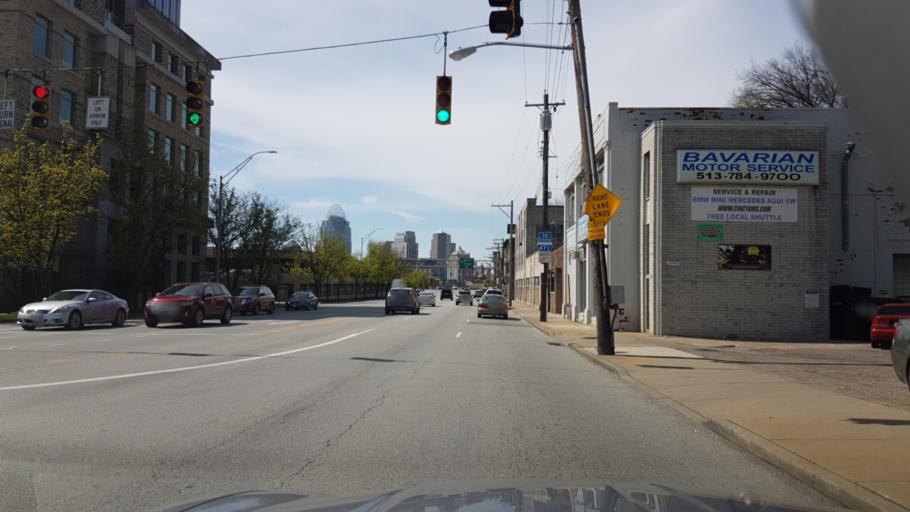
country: US
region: Kentucky
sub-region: Campbell County
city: Newport
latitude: 39.1135
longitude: -84.5023
